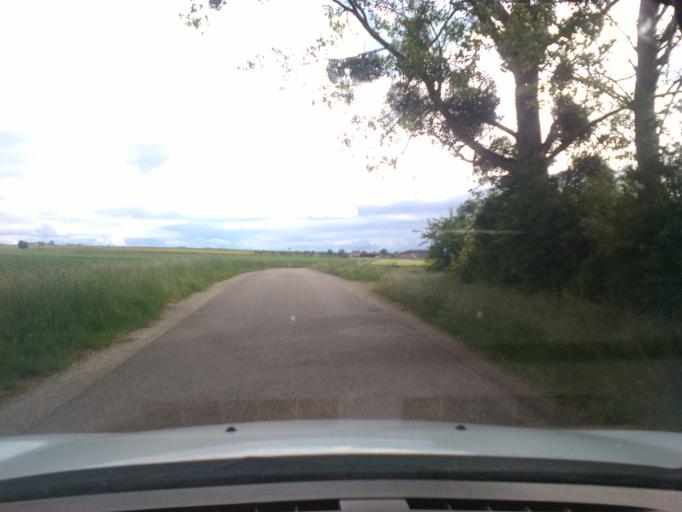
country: FR
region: Lorraine
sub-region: Departement des Vosges
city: Mirecourt
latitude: 48.3359
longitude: 6.0780
